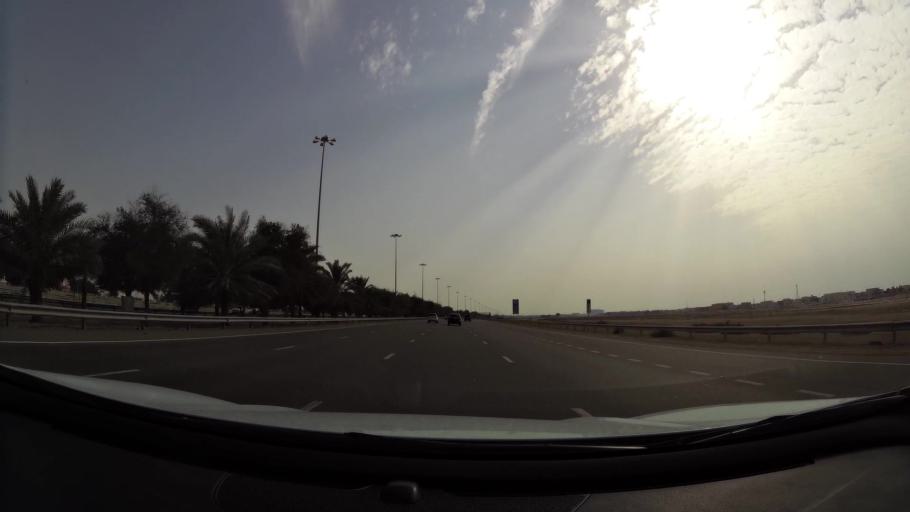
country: AE
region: Abu Dhabi
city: Abu Dhabi
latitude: 24.3650
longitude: 54.6521
